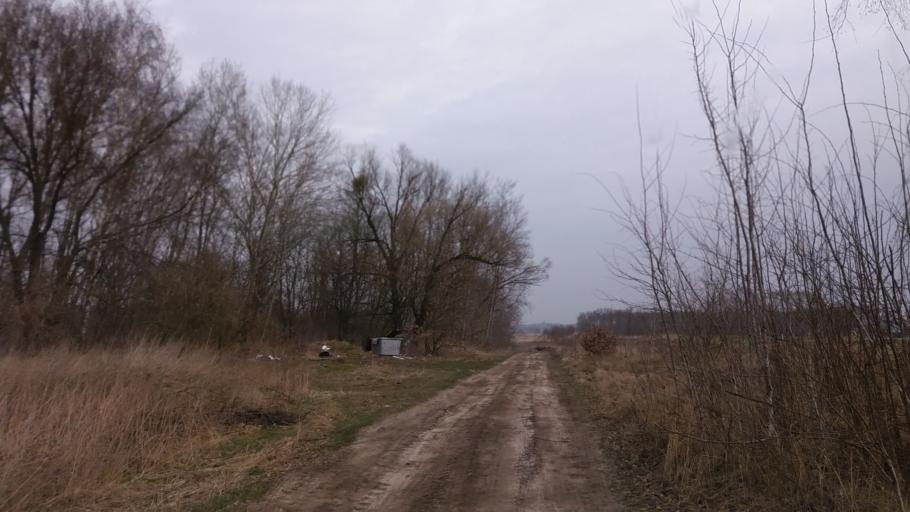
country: PL
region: West Pomeranian Voivodeship
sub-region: Powiat choszczenski
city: Pelczyce
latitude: 53.1122
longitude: 15.3386
